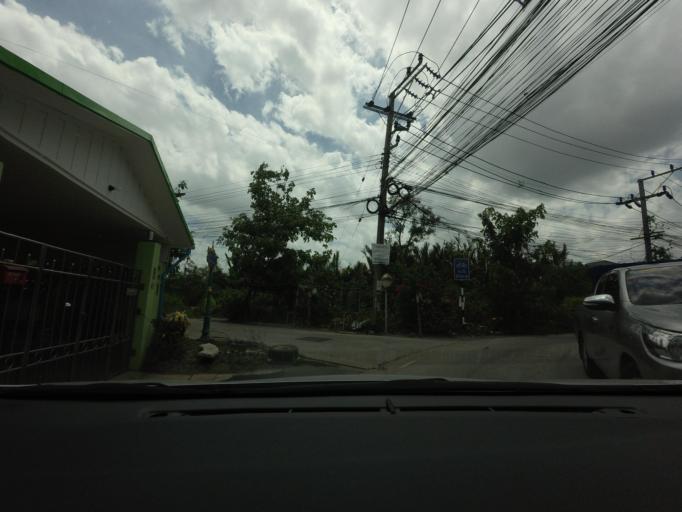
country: TH
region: Samut Prakan
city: Phra Samut Chedi
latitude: 13.6261
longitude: 100.5569
